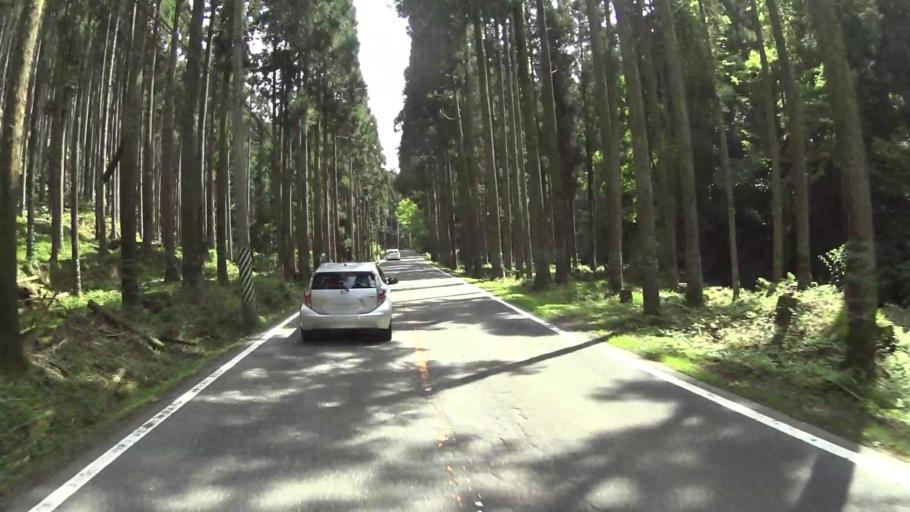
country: JP
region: Shiga Prefecture
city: Kitahama
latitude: 35.3714
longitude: 135.9216
